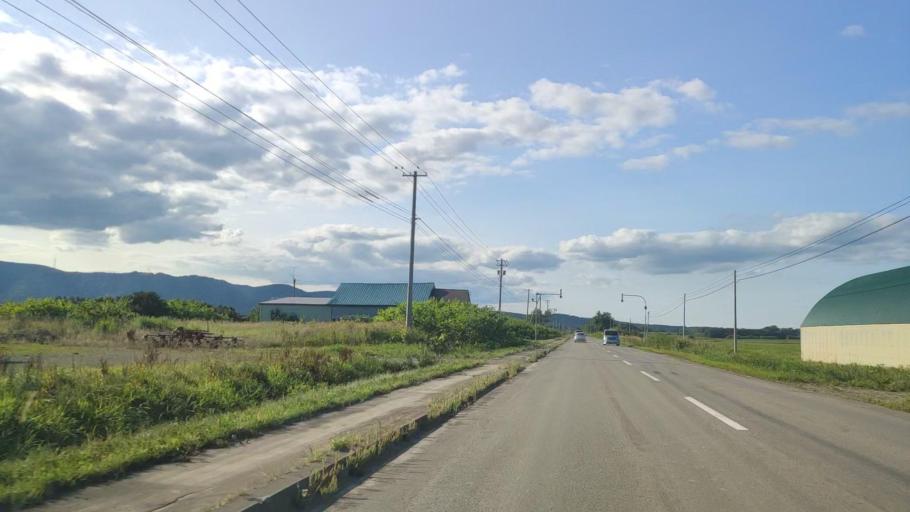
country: JP
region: Hokkaido
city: Makubetsu
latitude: 44.8246
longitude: 142.0643
